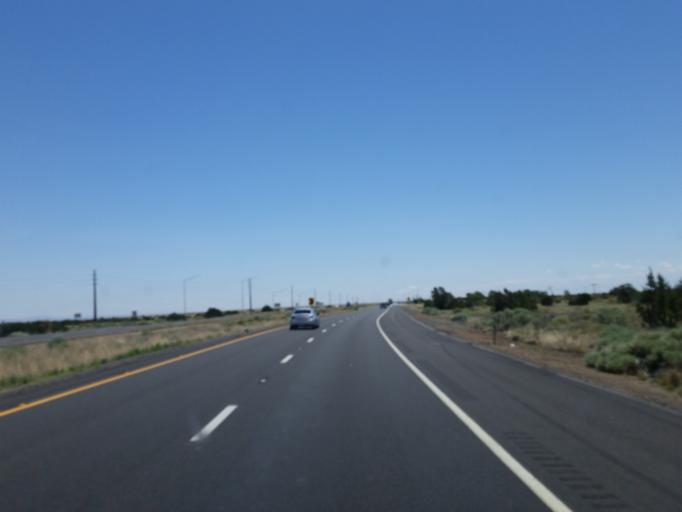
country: US
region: Arizona
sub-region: Coconino County
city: Flagstaff
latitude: 35.1612
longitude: -111.2718
